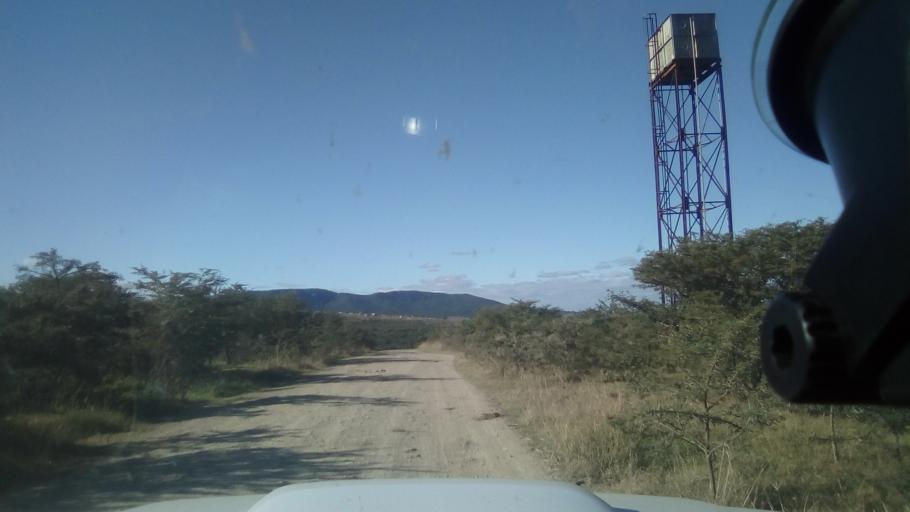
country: ZA
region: Eastern Cape
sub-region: Buffalo City Metropolitan Municipality
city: Bhisho
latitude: -32.7555
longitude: 27.3344
